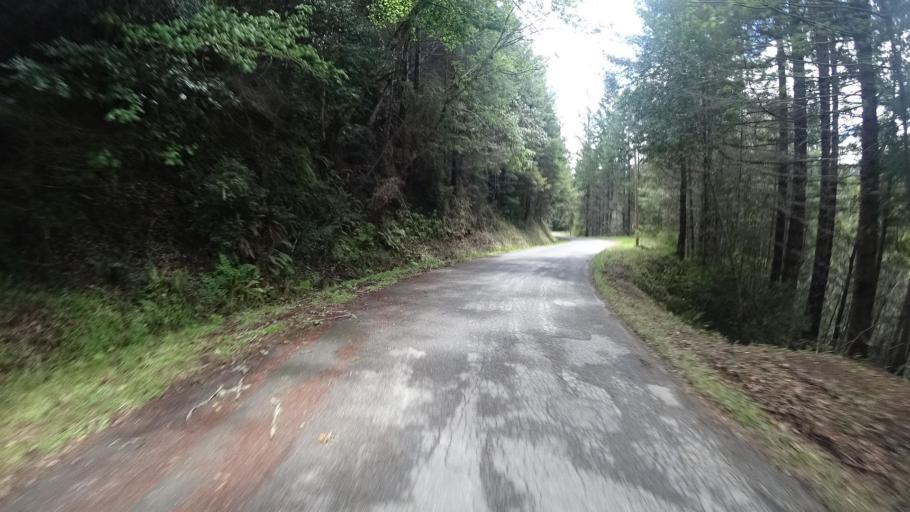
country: US
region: California
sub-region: Humboldt County
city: Blue Lake
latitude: 40.7661
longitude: -123.9287
